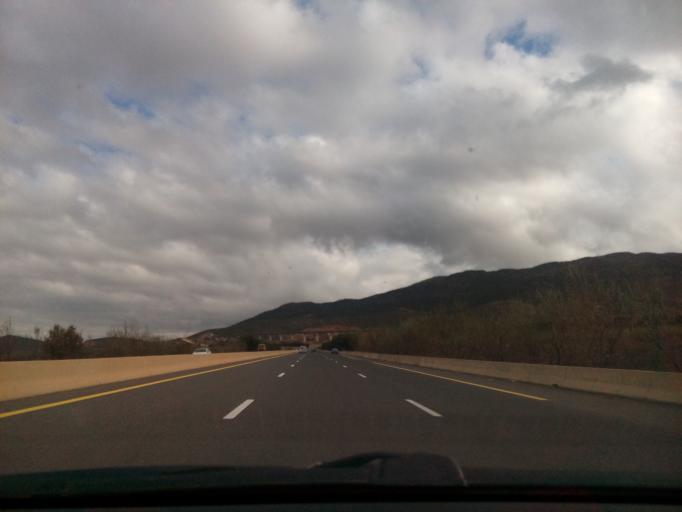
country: DZ
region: Tlemcen
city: Sidi Abdelli
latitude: 35.0096
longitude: -1.1738
